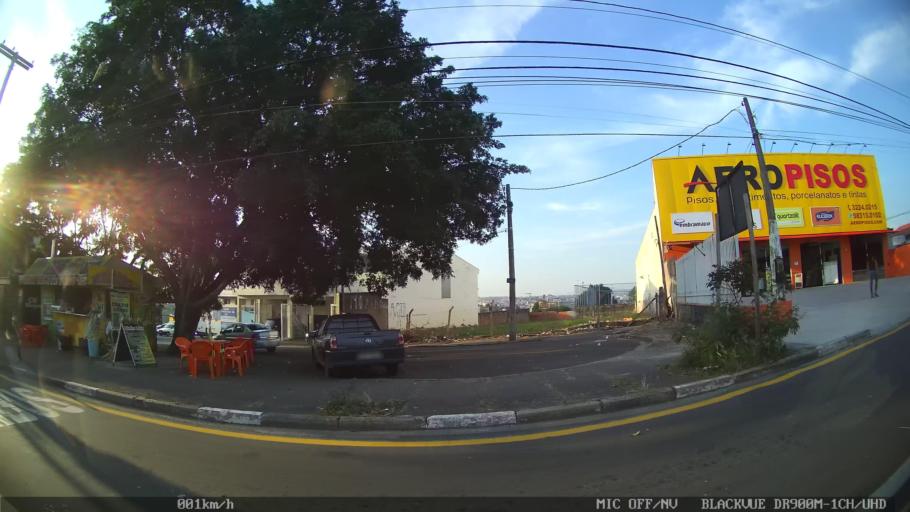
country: BR
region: Sao Paulo
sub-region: Campinas
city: Campinas
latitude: -22.9662
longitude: -47.1312
